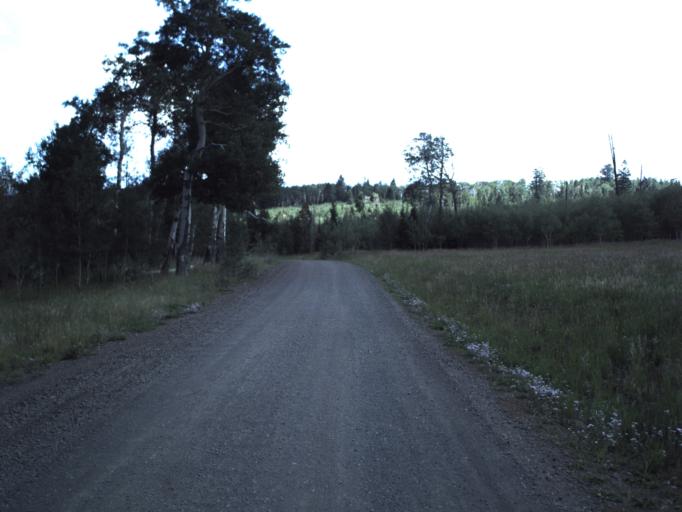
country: US
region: Utah
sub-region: Piute County
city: Junction
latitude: 38.2502
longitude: -112.3380
